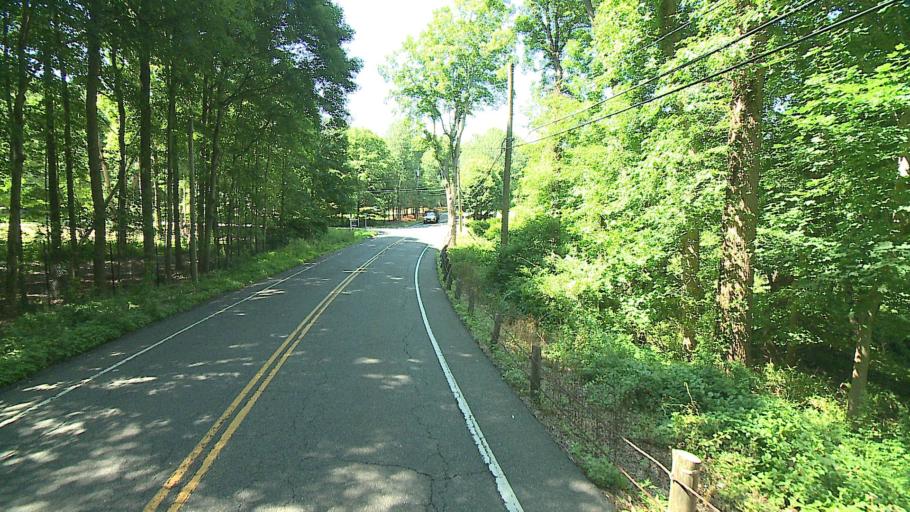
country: US
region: Connecticut
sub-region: Fairfield County
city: Ridgefield
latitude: 41.2572
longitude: -73.5157
